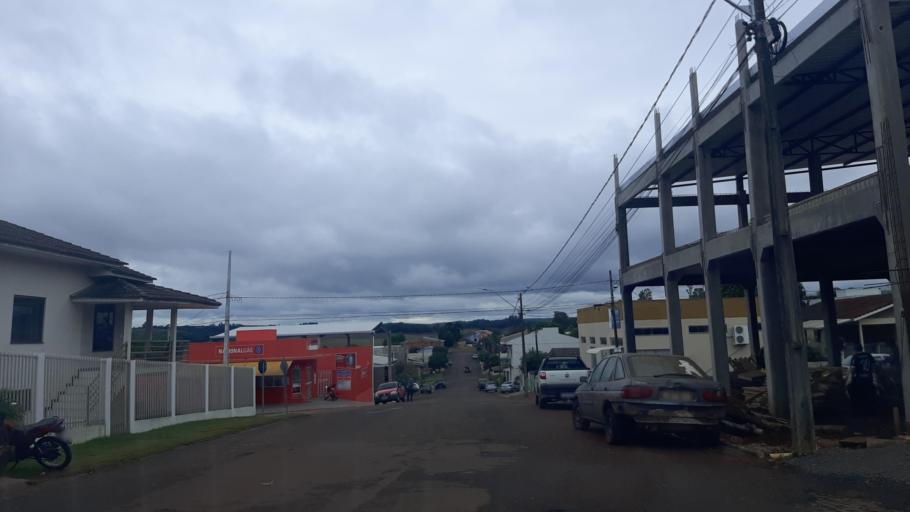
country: BR
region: Parana
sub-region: Ampere
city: Ampere
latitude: -25.9262
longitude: -53.4707
